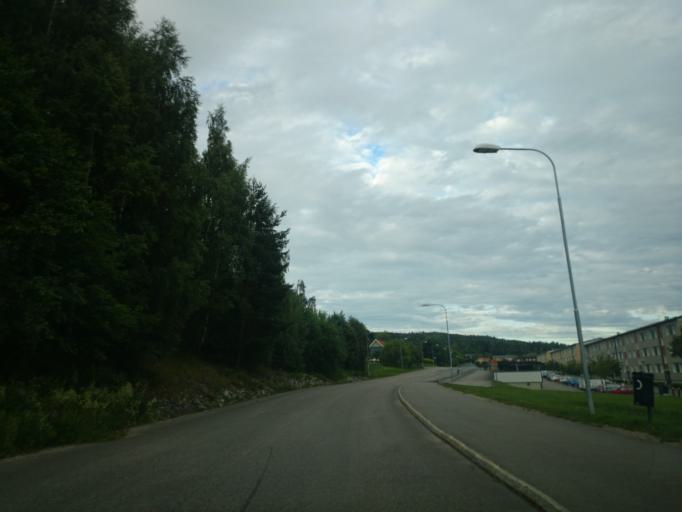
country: SE
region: Vaesternorrland
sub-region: Sundsvalls Kommun
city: Sundsvall
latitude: 62.4068
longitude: 17.2520
